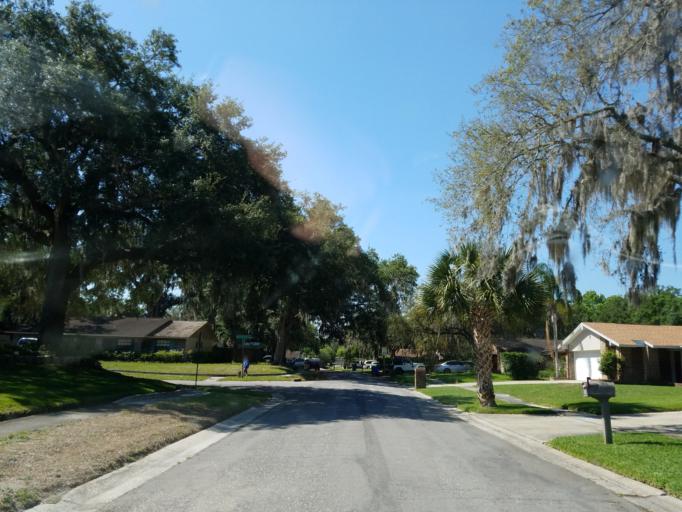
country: US
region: Florida
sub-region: Hillsborough County
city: Riverview
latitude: 27.8892
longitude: -82.2975
